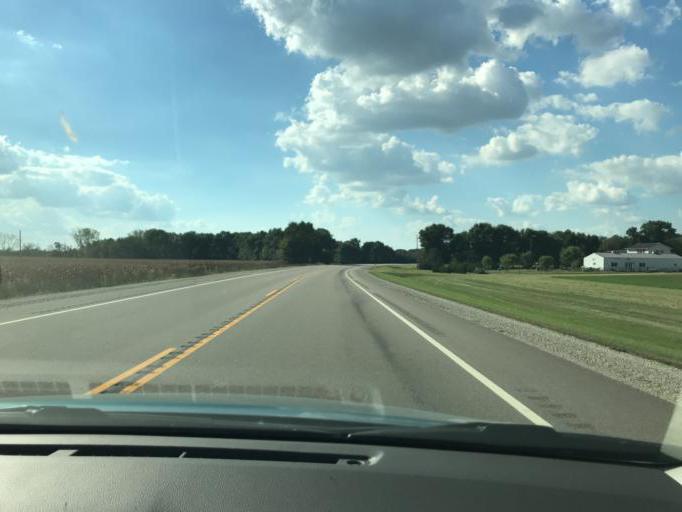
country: US
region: Wisconsin
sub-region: Green County
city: Brodhead
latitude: 42.5752
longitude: -89.3691
